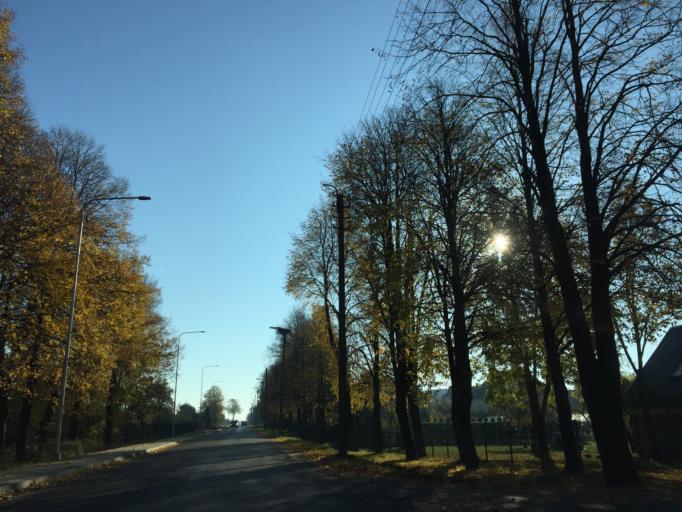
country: LT
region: Klaipedos apskritis
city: Kretinga
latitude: 55.8923
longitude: 21.2132
